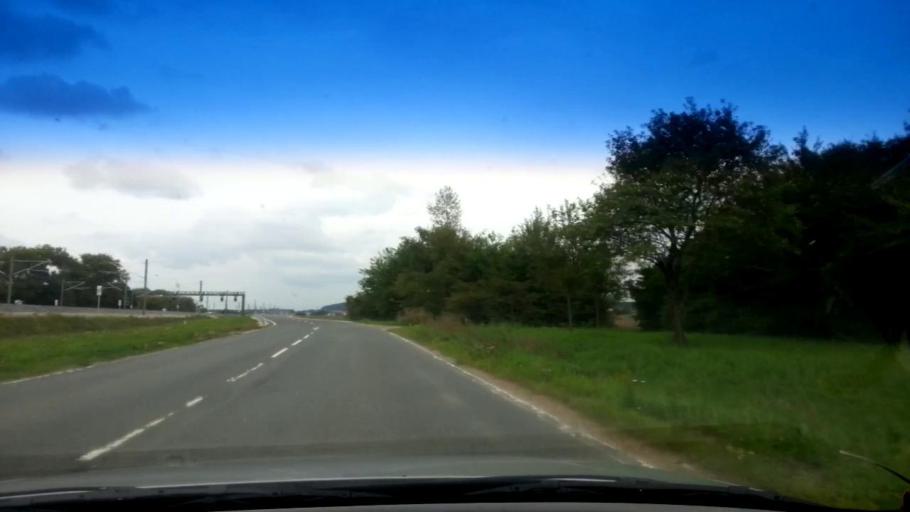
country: DE
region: Bavaria
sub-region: Upper Franconia
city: Zapfendorf
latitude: 50.0049
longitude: 10.9177
